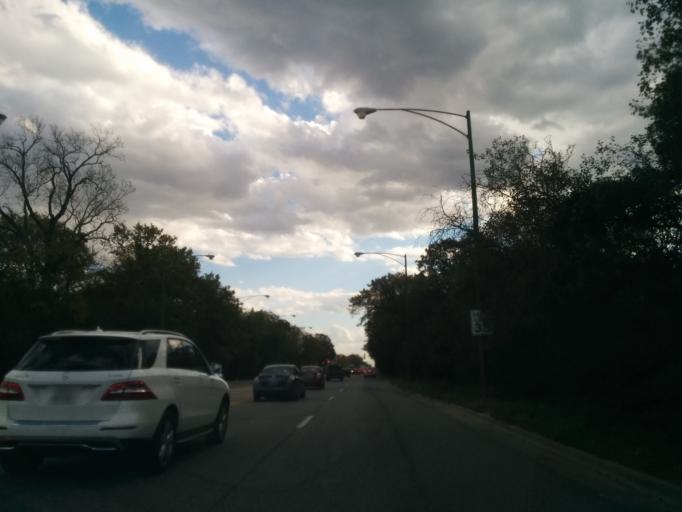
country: US
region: Illinois
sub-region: Cook County
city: River Grove
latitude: 41.9396
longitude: -87.8362
